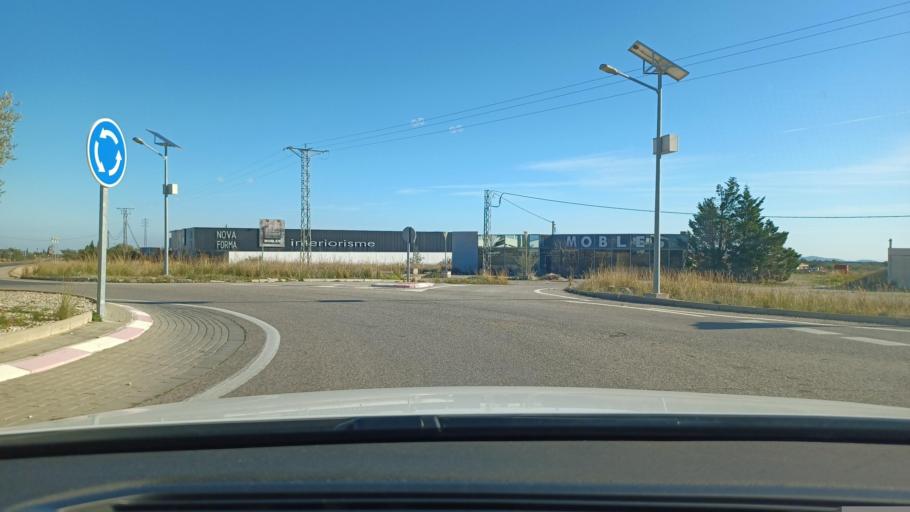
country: ES
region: Valencia
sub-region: Provincia de Castello
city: Rosell
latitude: 40.6340
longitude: 0.3131
